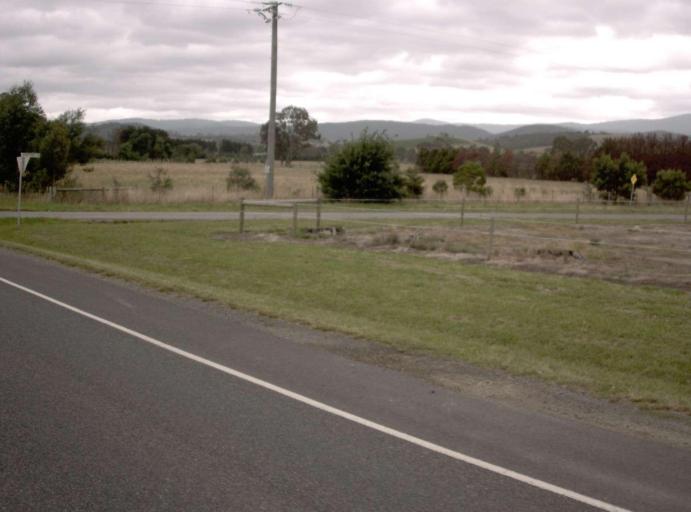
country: AU
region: Victoria
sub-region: Yarra Ranges
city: Yarra Glen
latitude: -37.6199
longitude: 145.4098
